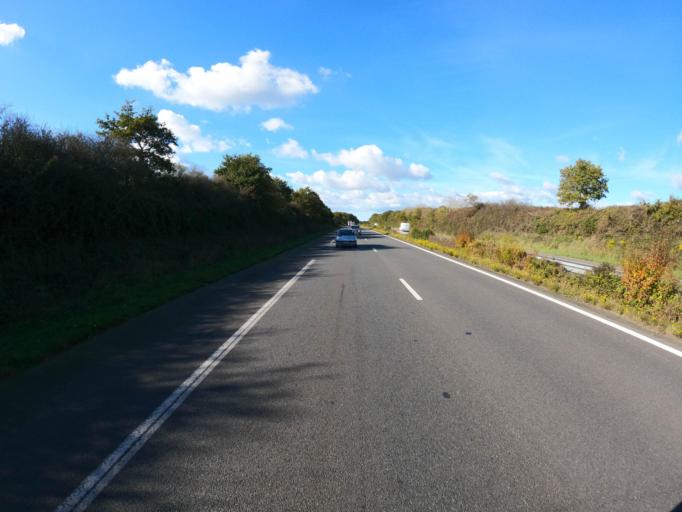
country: FR
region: Pays de la Loire
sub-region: Departement de la Loire-Atlantique
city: Pornichet
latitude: 47.2868
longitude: -2.3176
